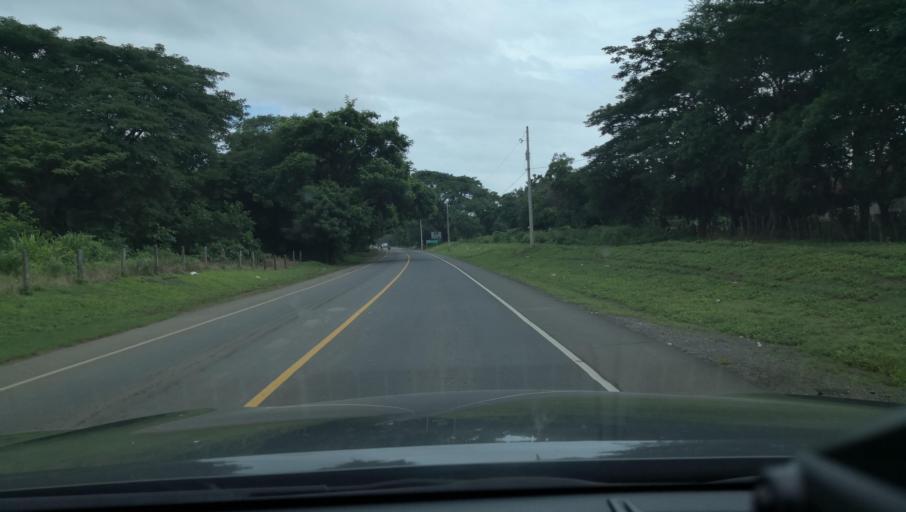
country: NI
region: Masaya
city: Nindiri
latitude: 12.0857
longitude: -86.1391
